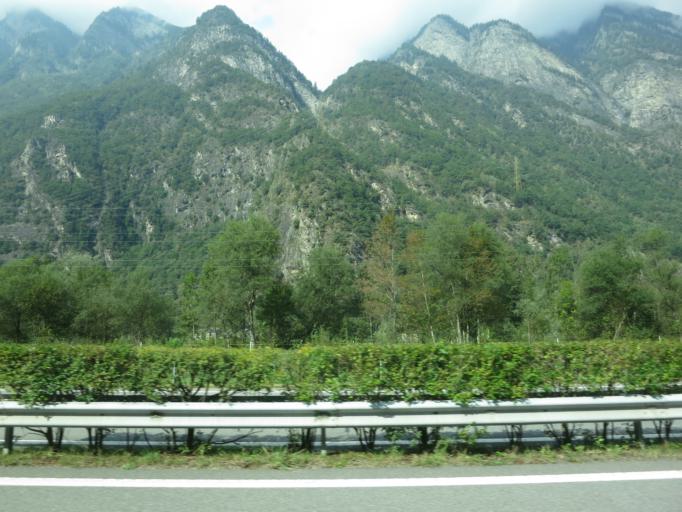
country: CH
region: Grisons
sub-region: Moesa District
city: Mesocco
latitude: 46.3213
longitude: 9.2059
